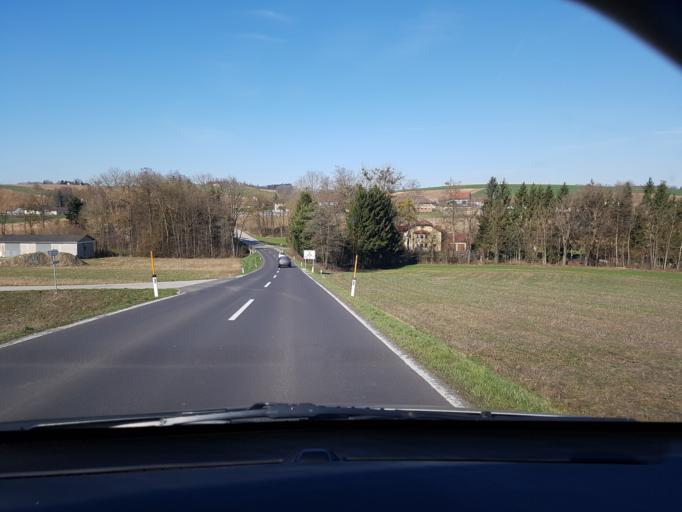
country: AT
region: Upper Austria
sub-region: Politischer Bezirk Linz-Land
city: Ansfelden
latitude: 48.1661
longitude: 14.3006
